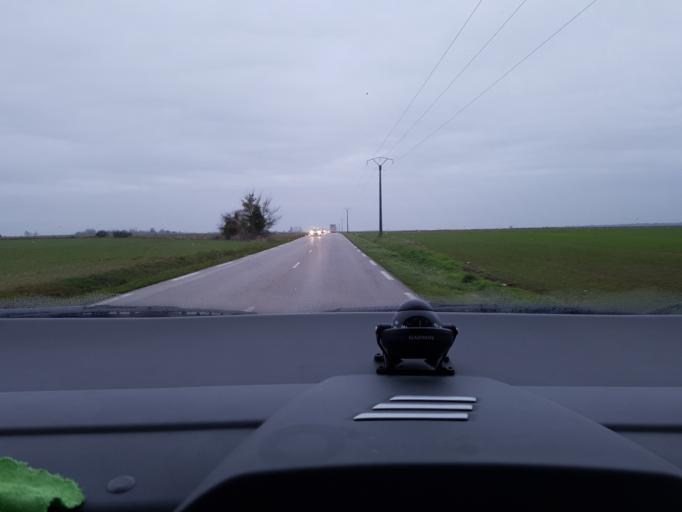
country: FR
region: Haute-Normandie
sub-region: Departement de l'Eure
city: Le Neubourg
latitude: 49.1503
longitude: 0.9737
